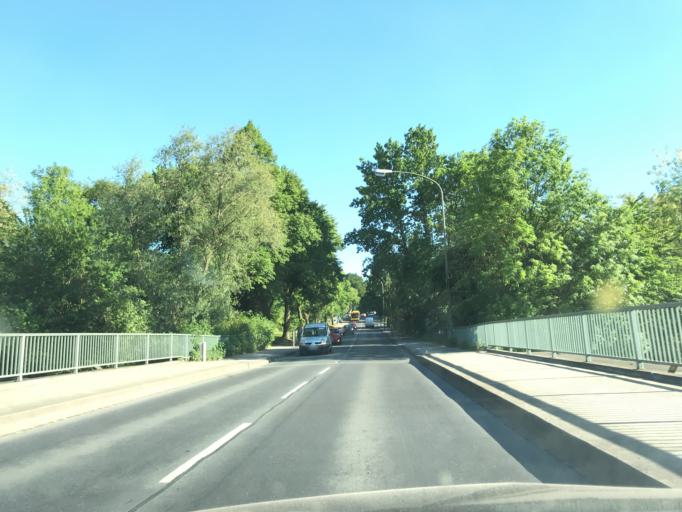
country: DE
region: North Rhine-Westphalia
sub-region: Regierungsbezirk Dusseldorf
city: Essen
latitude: 51.4673
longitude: 7.0453
